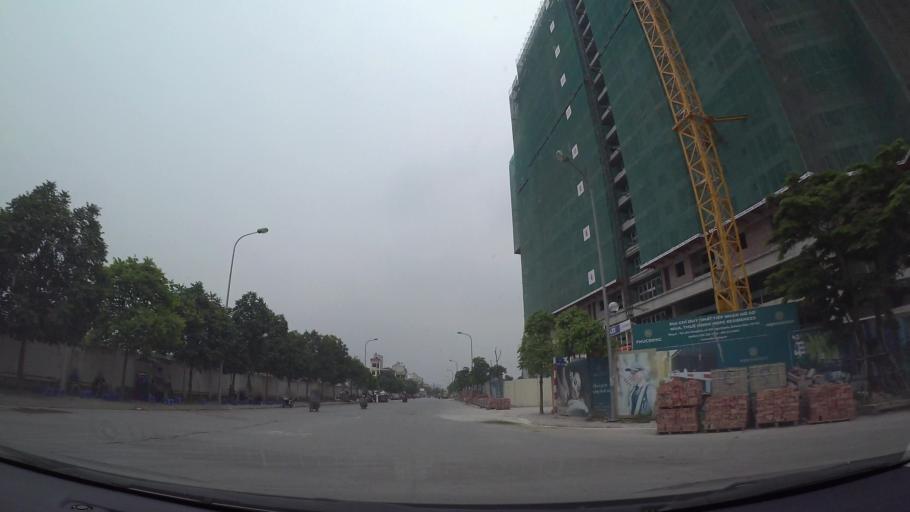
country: VN
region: Ha Noi
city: Trau Quy
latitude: 21.0411
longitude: 105.9043
